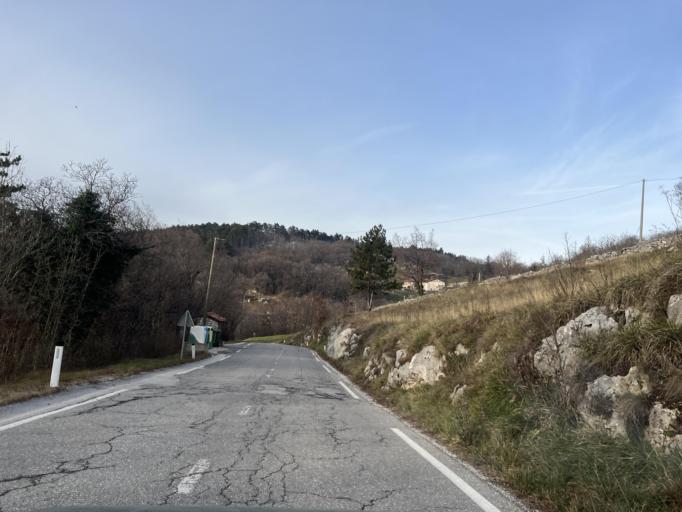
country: SI
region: Nova Gorica
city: Kromberk
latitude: 45.9832
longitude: 13.7122
